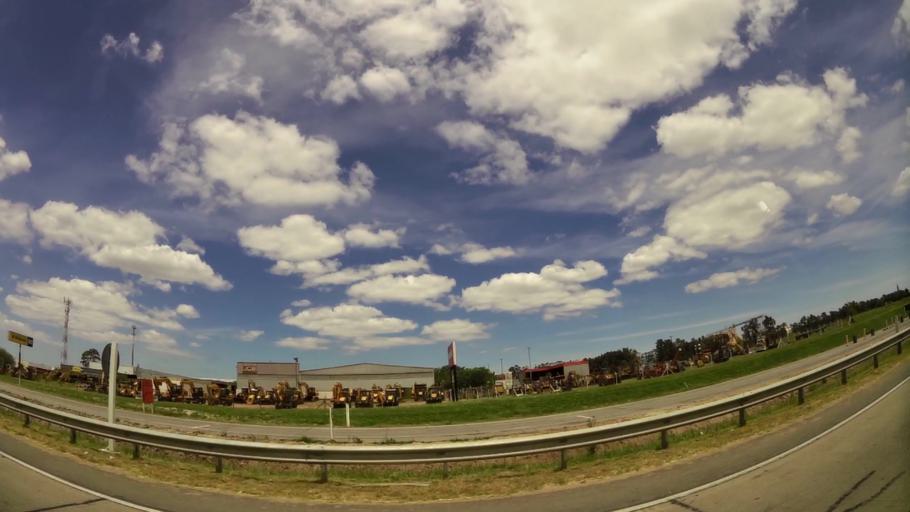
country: UY
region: Montevideo
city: Pajas Blancas
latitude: -34.8536
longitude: -56.2779
